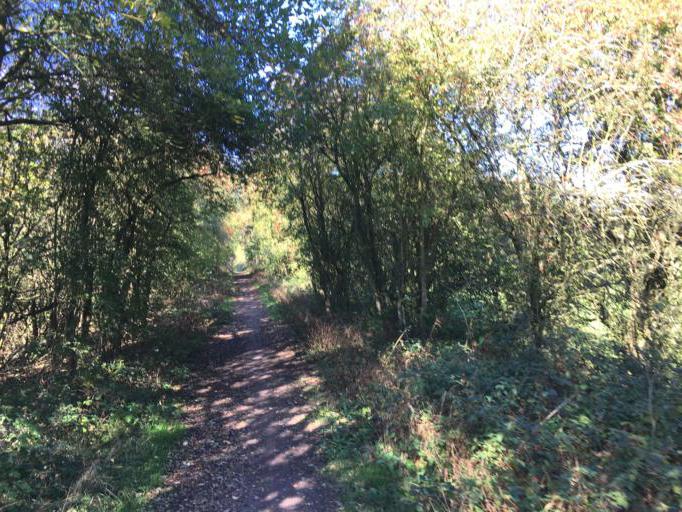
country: GB
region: England
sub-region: Solihull
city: Balsall Common
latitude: 52.3917
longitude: -1.6309
